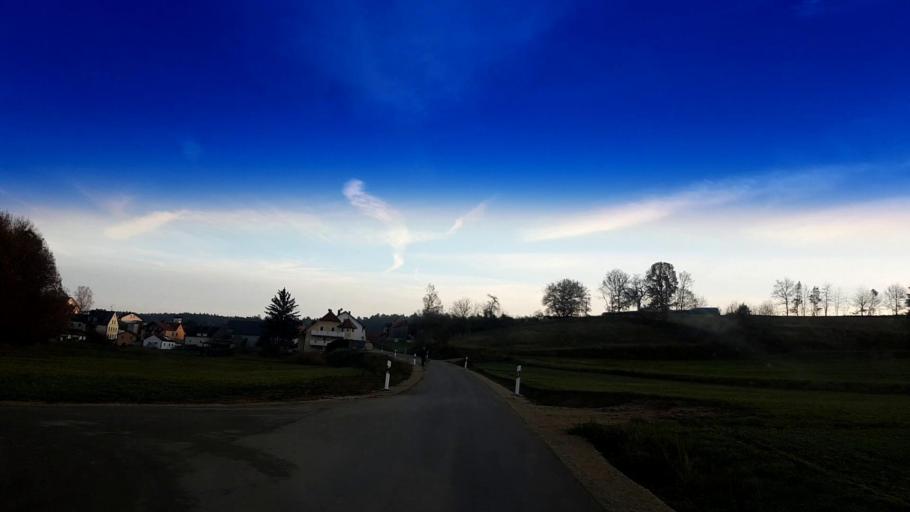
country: DE
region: Bavaria
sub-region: Upper Franconia
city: Walsdorf
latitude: 49.8641
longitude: 10.7979
